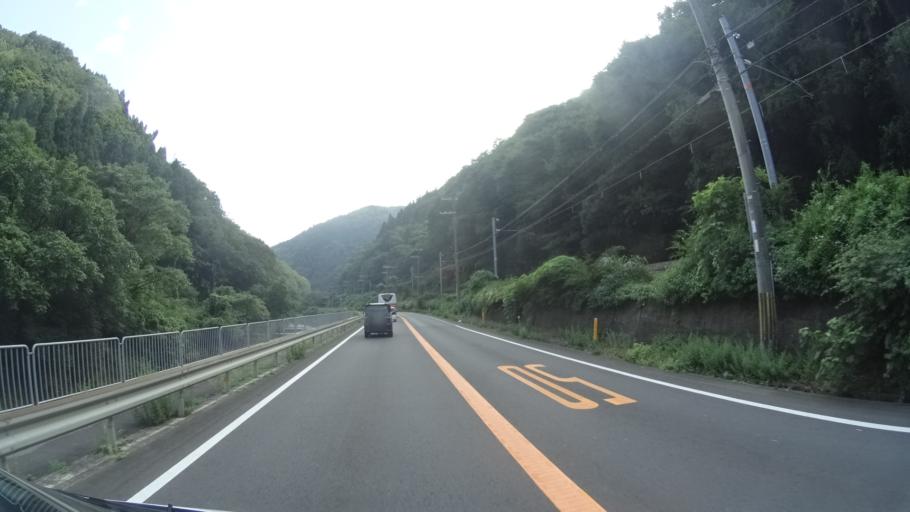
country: JP
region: Kyoto
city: Maizuru
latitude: 35.3889
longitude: 135.3160
